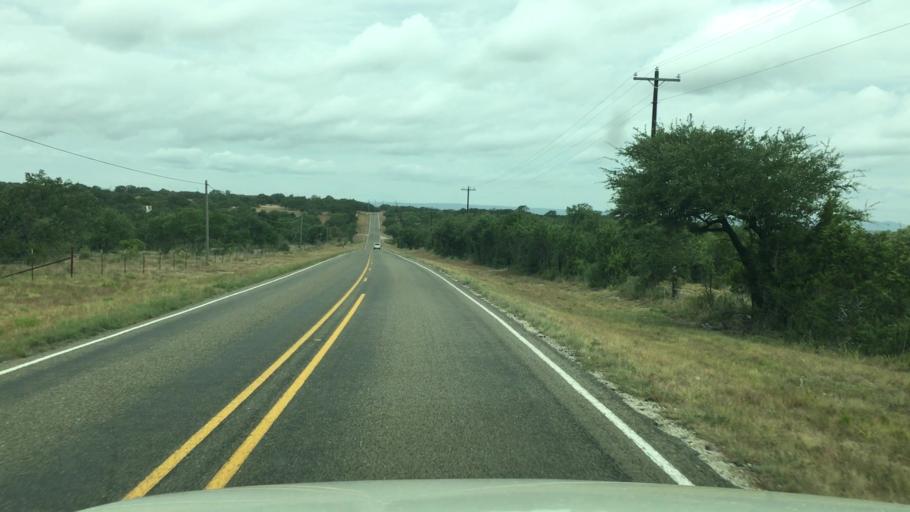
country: US
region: Texas
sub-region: Llano County
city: Horseshoe Bay
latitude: 30.4612
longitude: -98.4025
